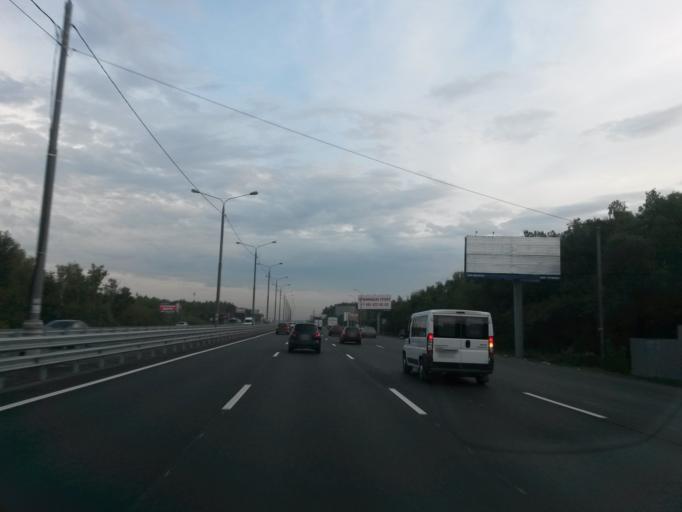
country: RU
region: Moskovskaya
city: Shcherbinka
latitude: 55.4959
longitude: 37.6107
